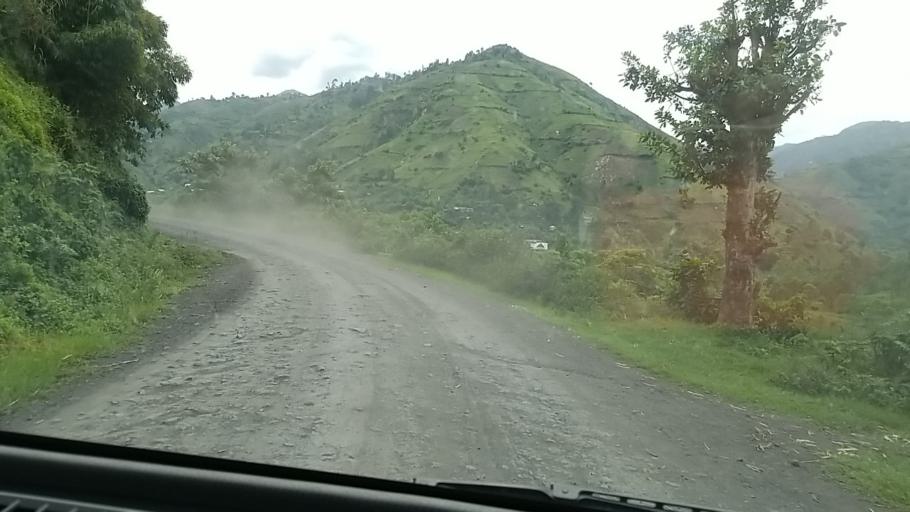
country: CD
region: Nord Kivu
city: Sake
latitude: -1.7423
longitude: 28.9916
